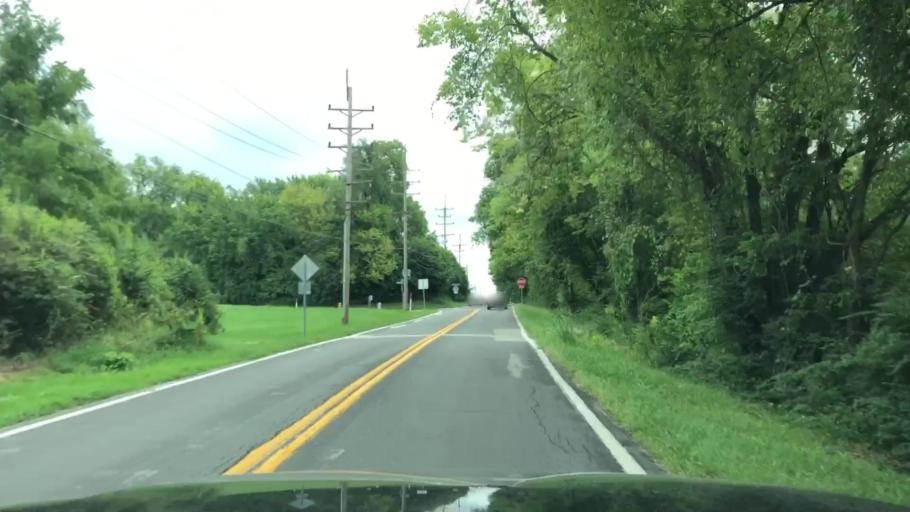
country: US
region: Missouri
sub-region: Saint Louis County
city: Hazelwood
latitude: 38.8147
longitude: -90.3684
